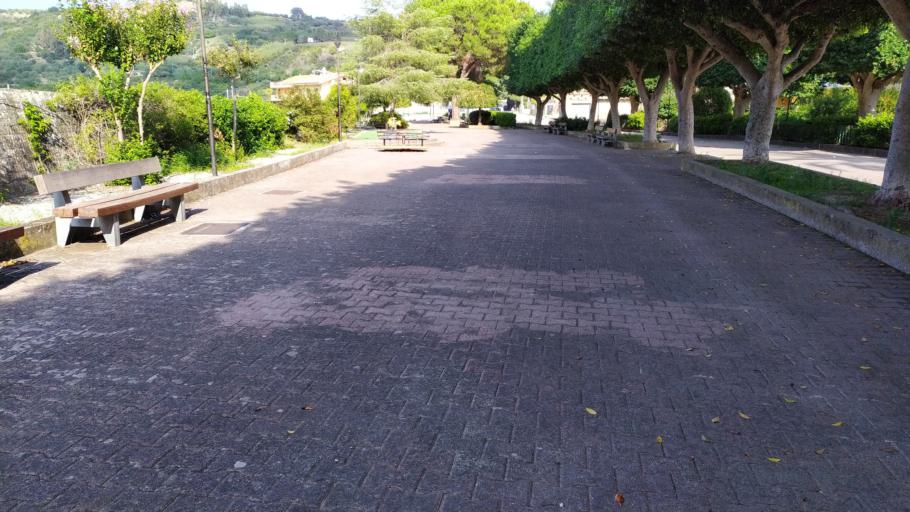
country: IT
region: Sicily
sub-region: Messina
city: Gualtieri Sicamino
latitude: 38.1645
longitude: 15.3192
